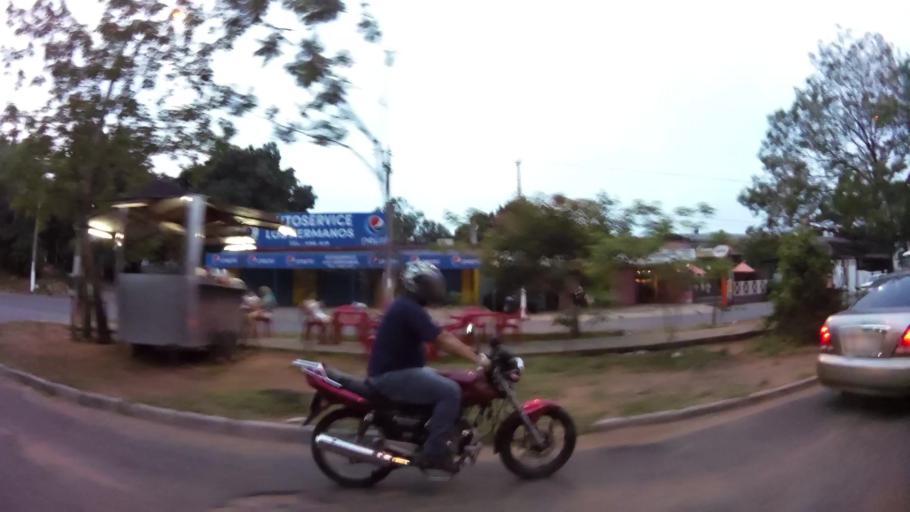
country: PY
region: Central
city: Lambare
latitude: -25.3295
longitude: -57.6003
